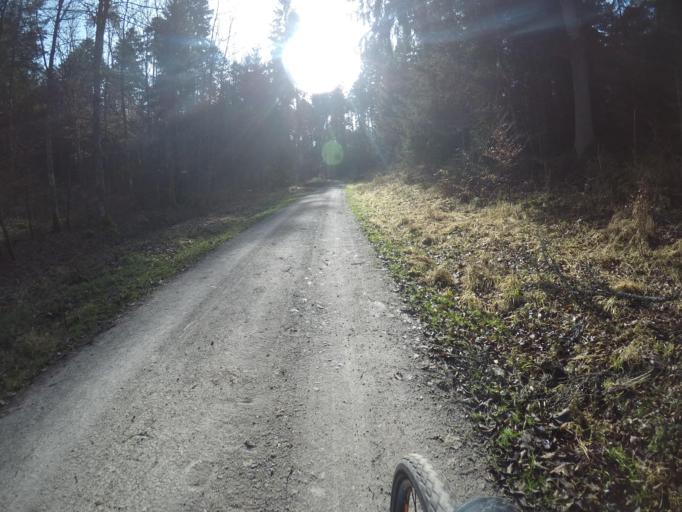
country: DE
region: Baden-Wuerttemberg
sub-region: Regierungsbezirk Stuttgart
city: Oberjettingen
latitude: 48.5928
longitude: 8.7948
